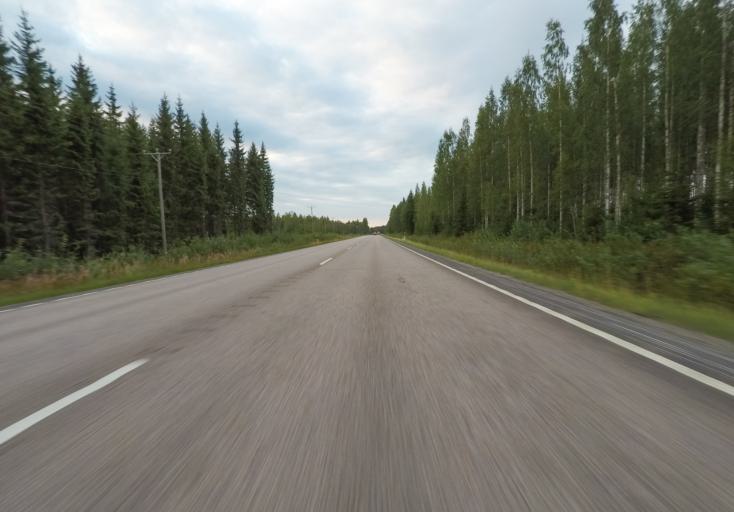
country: FI
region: Central Finland
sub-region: Joutsa
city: Leivonmaeki
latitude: 61.9272
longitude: 26.1156
